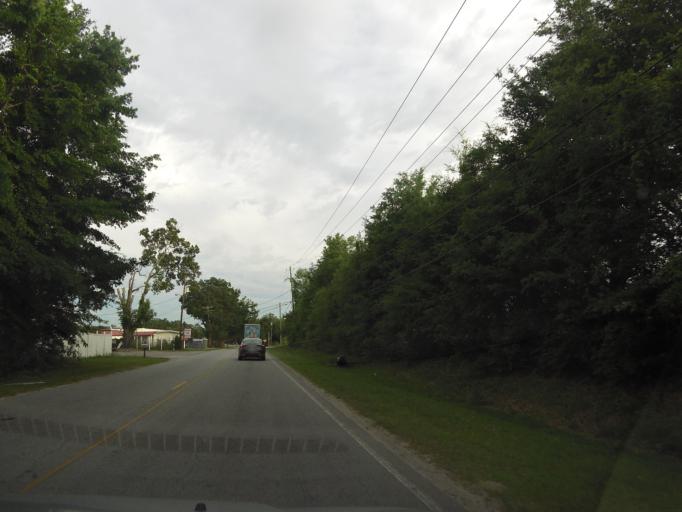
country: US
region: Georgia
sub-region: Chatham County
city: Garden City
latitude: 32.0884
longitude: -81.1988
